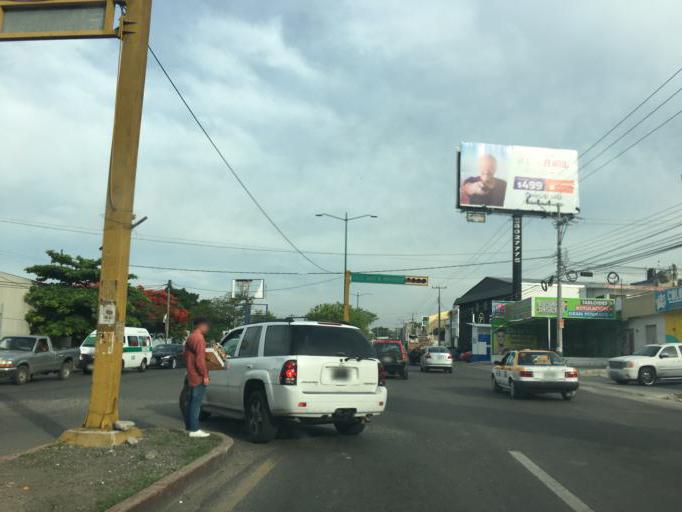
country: MX
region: Chiapas
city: Tuxtla Gutierrez
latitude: 16.7618
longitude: -93.1511
